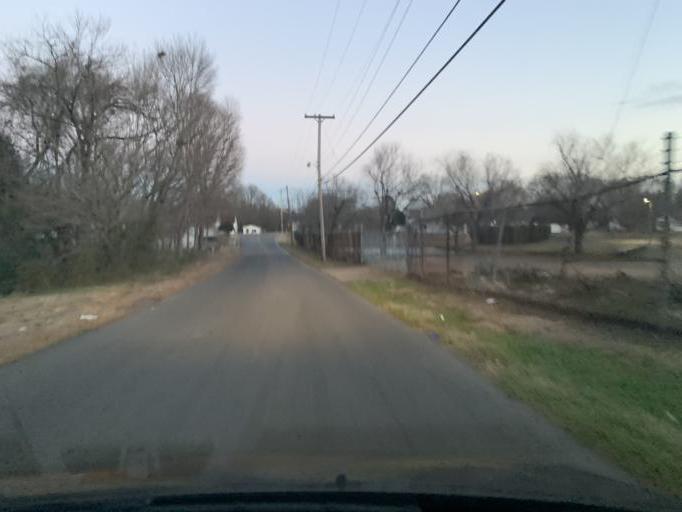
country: US
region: North Carolina
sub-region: Cleveland County
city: Shelby
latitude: 35.2706
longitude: -81.5425
